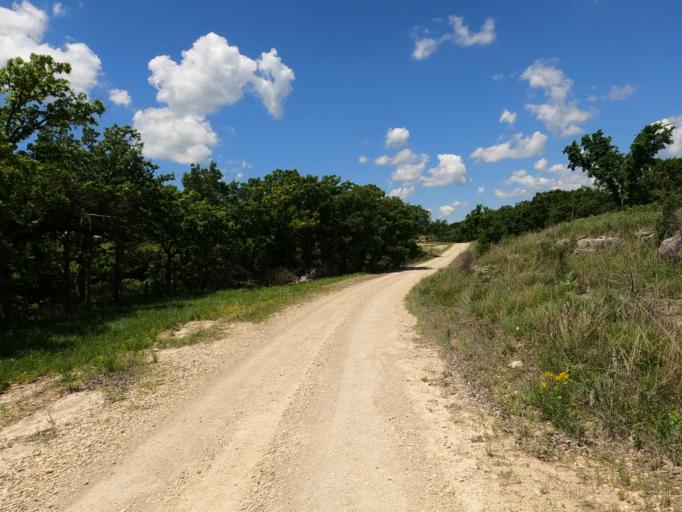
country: US
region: Kansas
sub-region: Marion County
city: Marion
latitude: 38.2410
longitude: -96.8005
